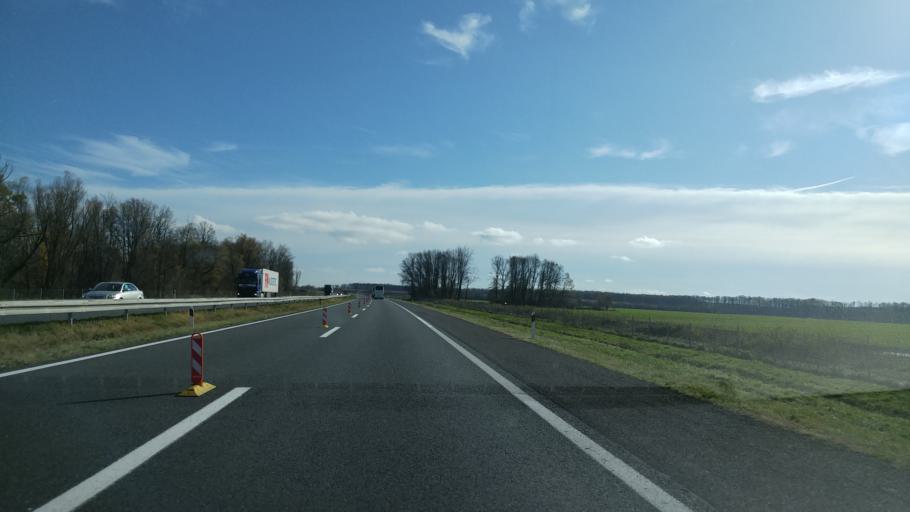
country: HR
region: Sisacko-Moslavacka
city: Lipovljani
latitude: 45.3798
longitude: 16.8742
